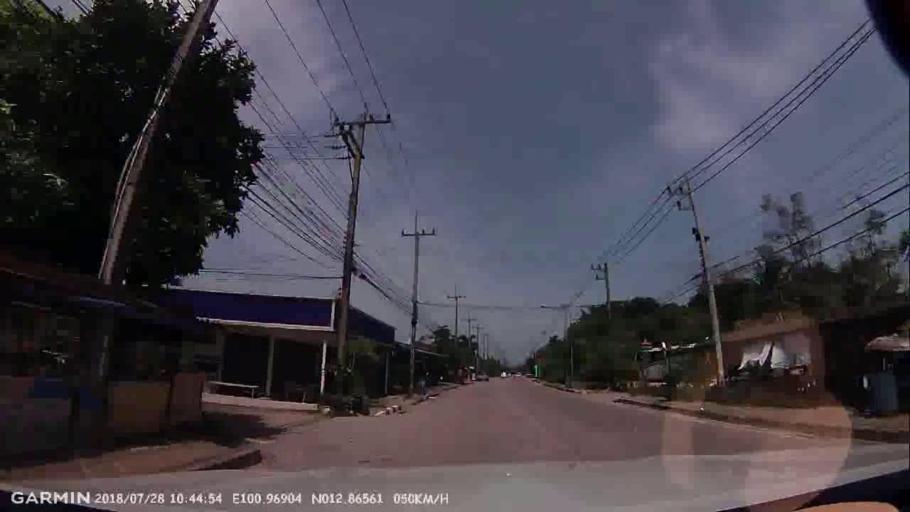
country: TH
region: Chon Buri
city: Phatthaya
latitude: 12.8656
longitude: 100.9690
